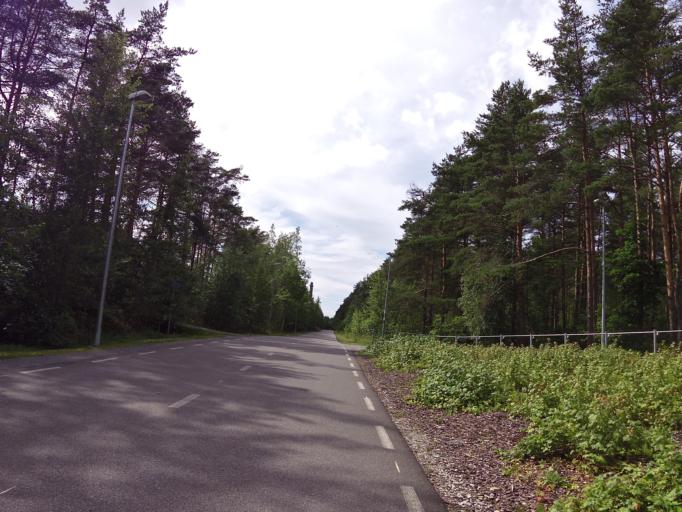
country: EE
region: Harju
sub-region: Saue vald
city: Laagri
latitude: 59.3837
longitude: 24.6486
